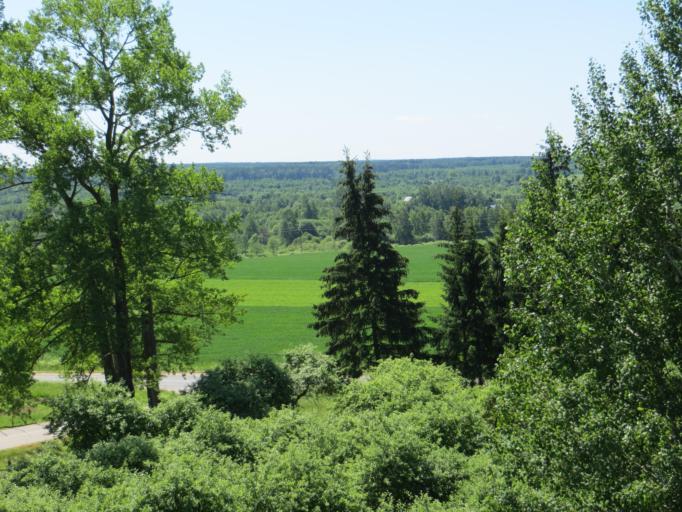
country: LT
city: Sirvintos
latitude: 54.9374
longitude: 25.0125
